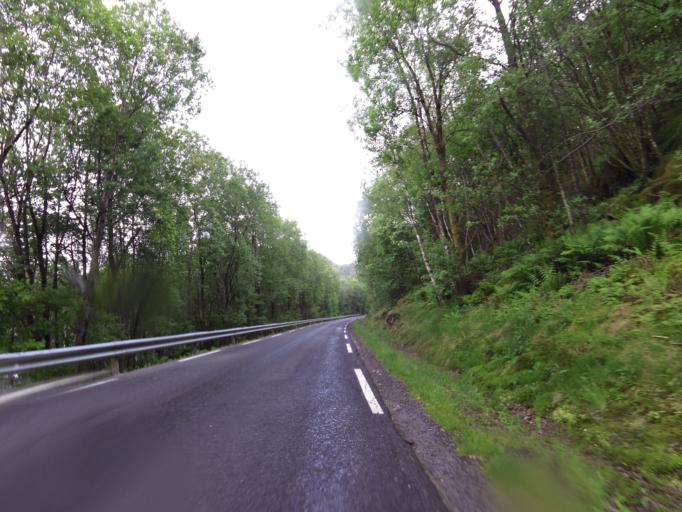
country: NO
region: Vest-Agder
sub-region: Lyngdal
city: Lyngdal
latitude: 58.1148
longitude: 7.0780
